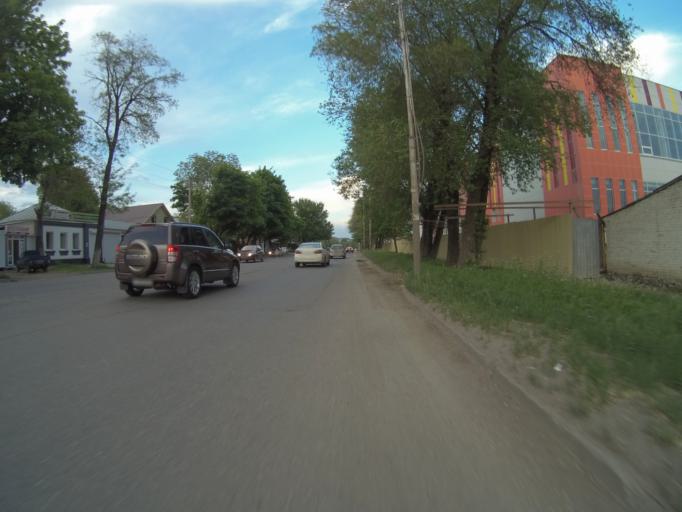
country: RU
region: Stavropol'skiy
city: Svobody
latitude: 44.0404
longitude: 43.0376
